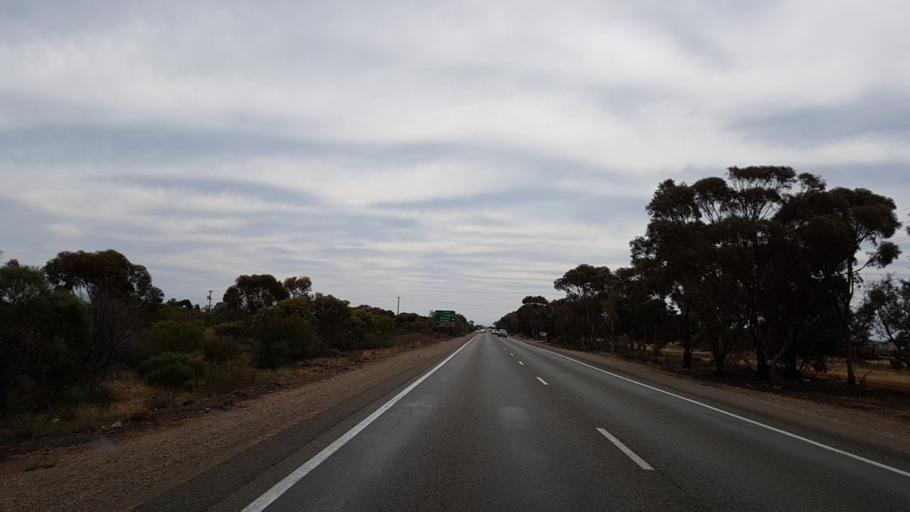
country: AU
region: South Australia
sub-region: Port Pirie City and Dists
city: Solomontown
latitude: -33.2254
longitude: 138.1091
